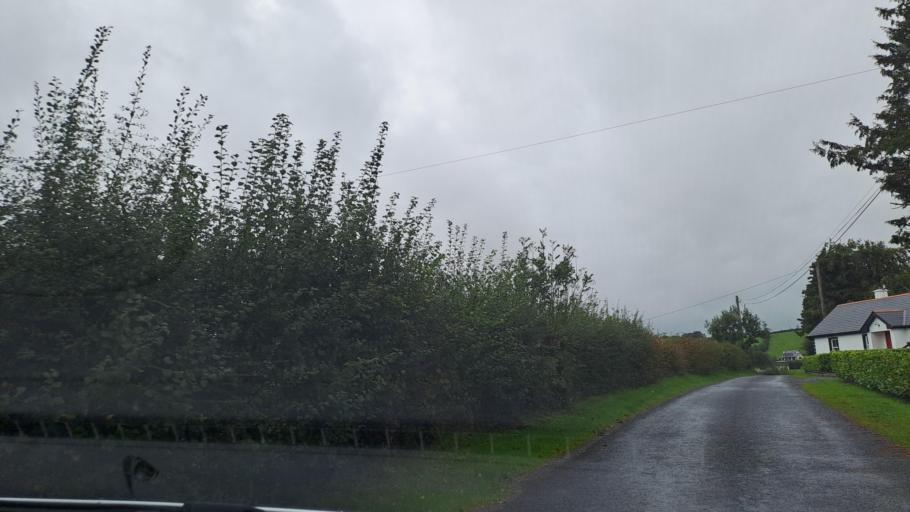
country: IE
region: Ulster
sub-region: An Cabhan
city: Kingscourt
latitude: 53.9360
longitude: -6.8575
